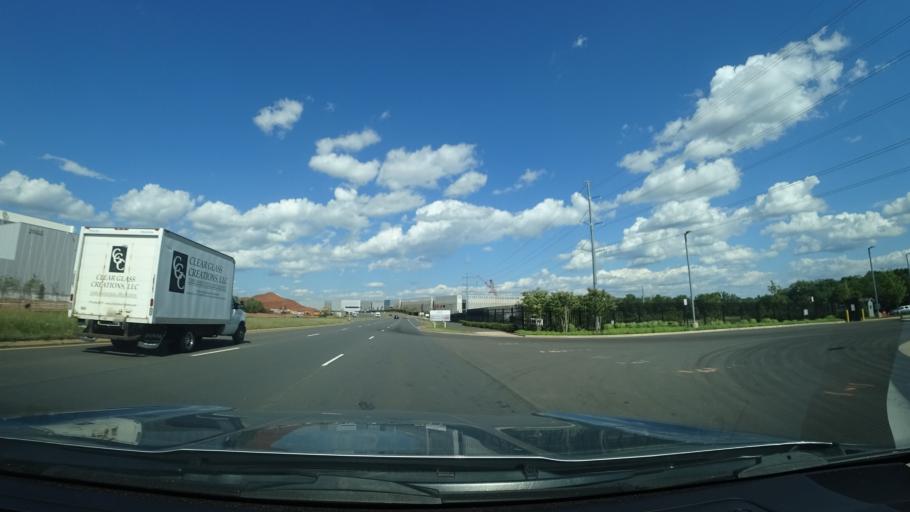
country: US
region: Virginia
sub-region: Loudoun County
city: Sterling
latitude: 39.0089
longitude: -77.4642
